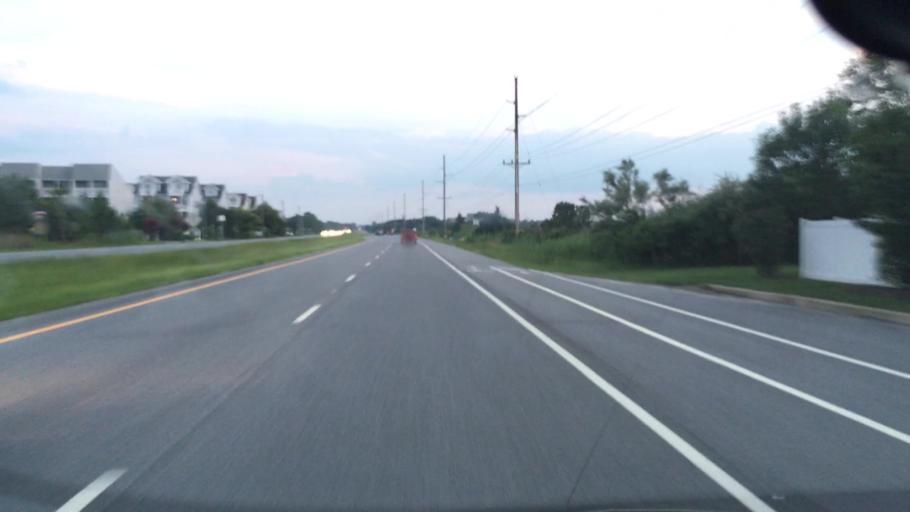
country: US
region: Delaware
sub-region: Sussex County
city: Bethany Beach
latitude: 38.5893
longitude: -75.0621
